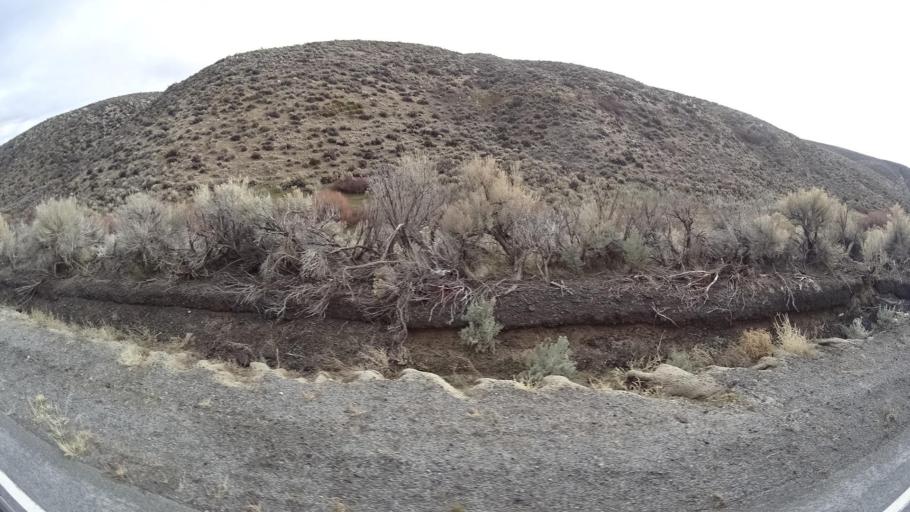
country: US
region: Nevada
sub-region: Washoe County
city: Cold Springs
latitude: 39.8183
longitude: -119.9360
